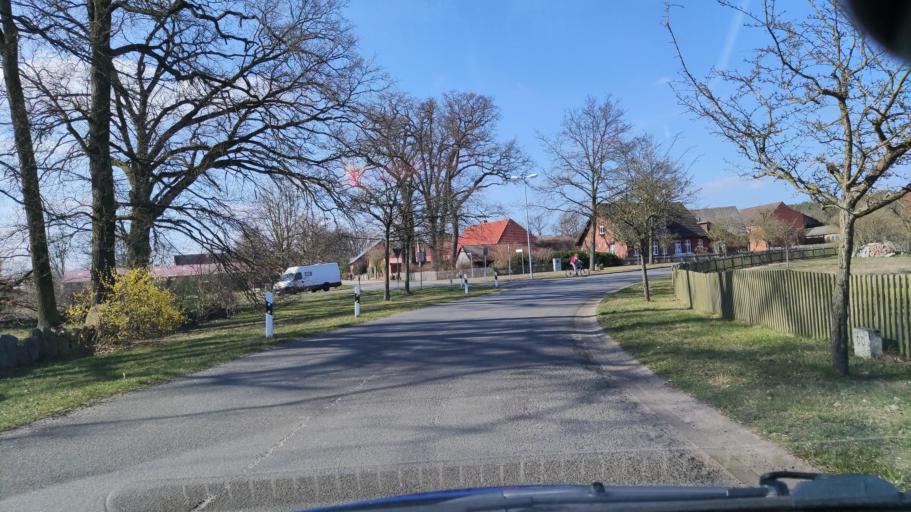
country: DE
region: Lower Saxony
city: Klein Gusborn
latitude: 53.0767
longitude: 11.2174
